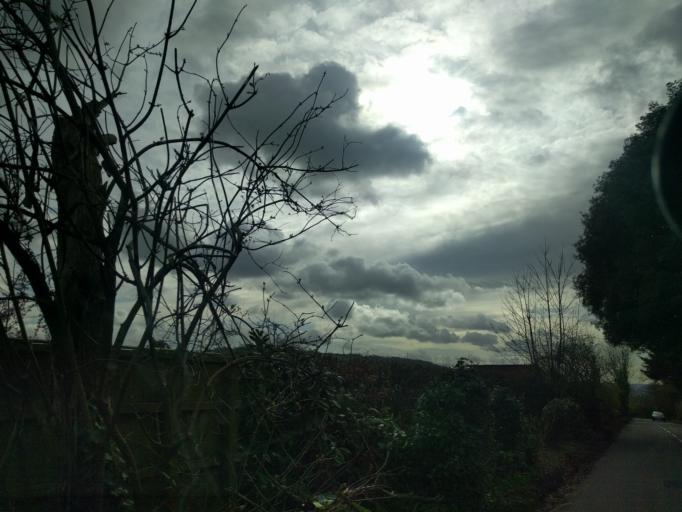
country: GB
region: England
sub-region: Wiltshire
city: Colerne
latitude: 51.4076
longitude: -2.3081
